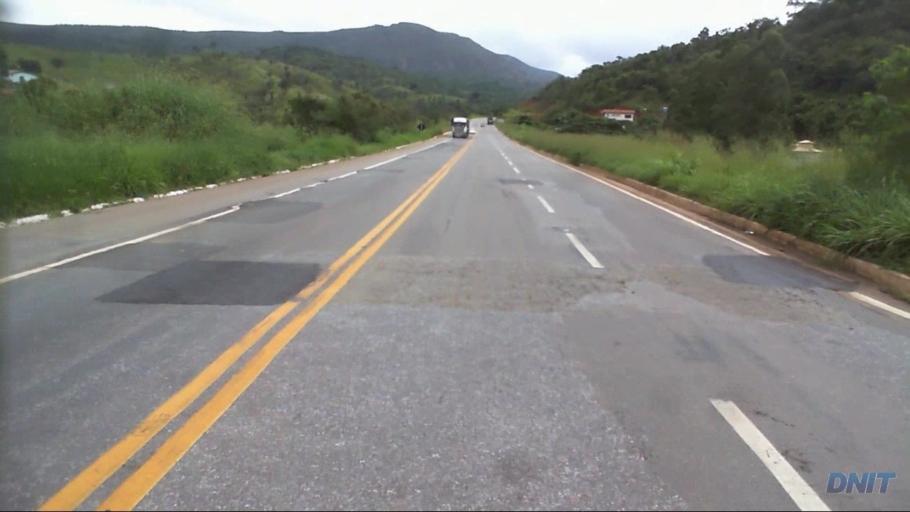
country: BR
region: Minas Gerais
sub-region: Barao De Cocais
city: Barao de Cocais
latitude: -19.8315
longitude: -43.3581
